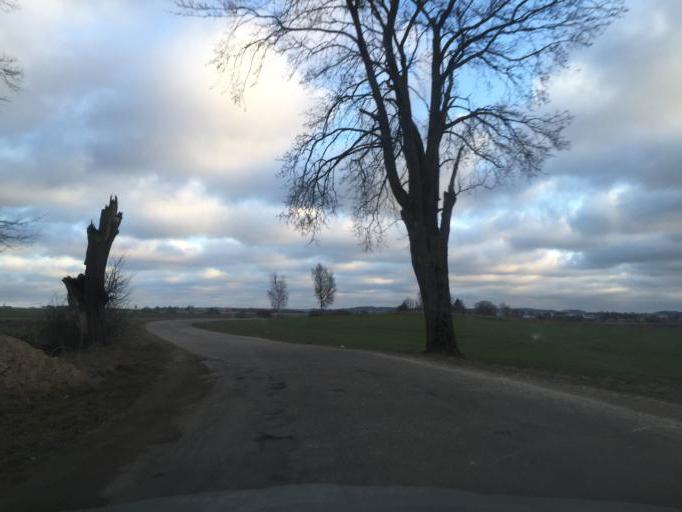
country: PL
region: Pomeranian Voivodeship
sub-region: Powiat kartuski
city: Banino
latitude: 54.4009
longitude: 18.4322
